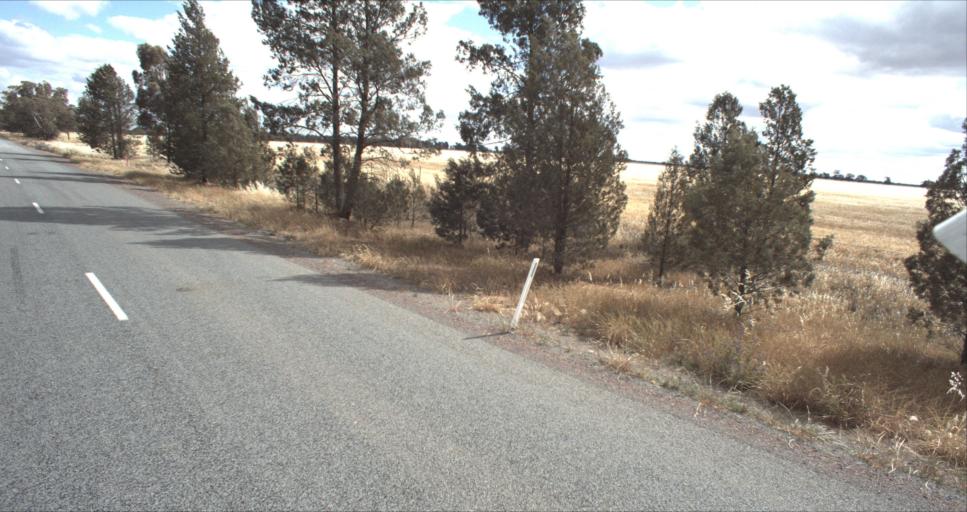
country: AU
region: New South Wales
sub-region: Leeton
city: Leeton
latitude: -34.6753
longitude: 146.3467
